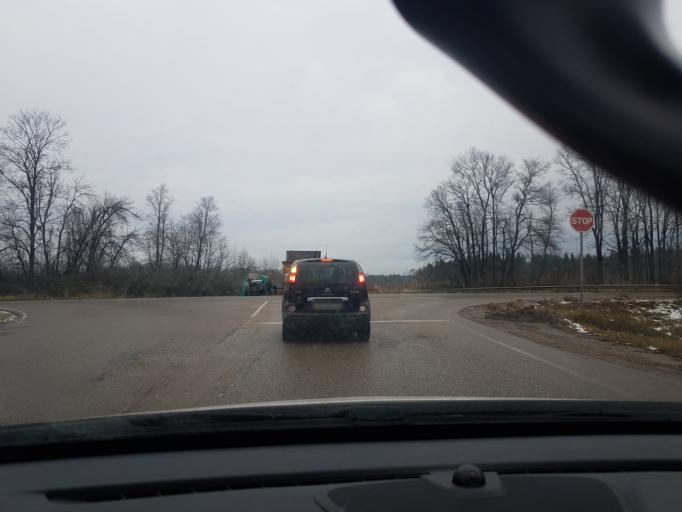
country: RU
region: Moskovskaya
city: Sychevo
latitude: 56.0071
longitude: 36.2381
